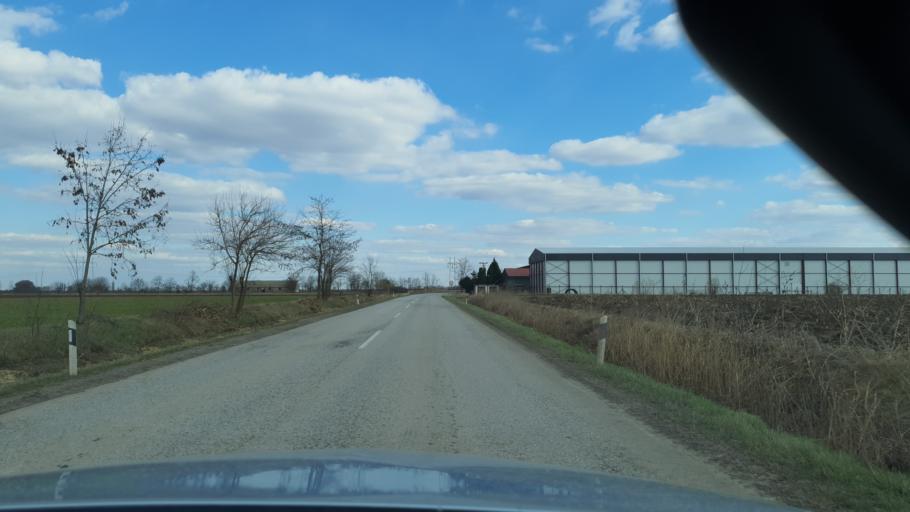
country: RS
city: Zmajevo
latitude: 45.4467
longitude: 19.7156
